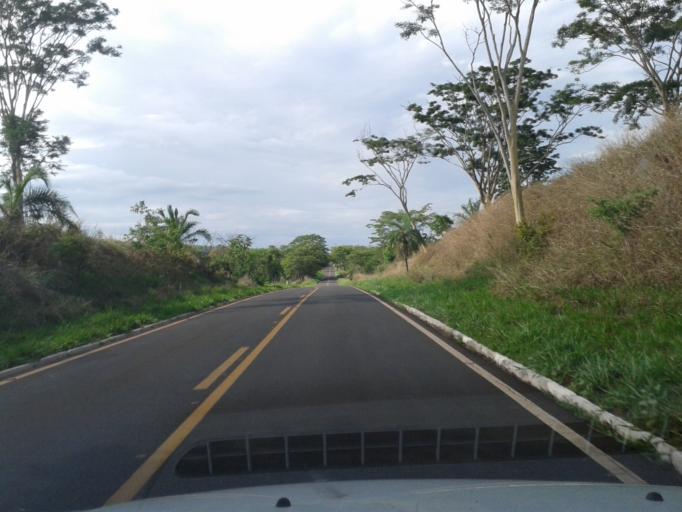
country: BR
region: Minas Gerais
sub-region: Ituiutaba
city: Ituiutaba
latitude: -19.1755
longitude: -49.7806
